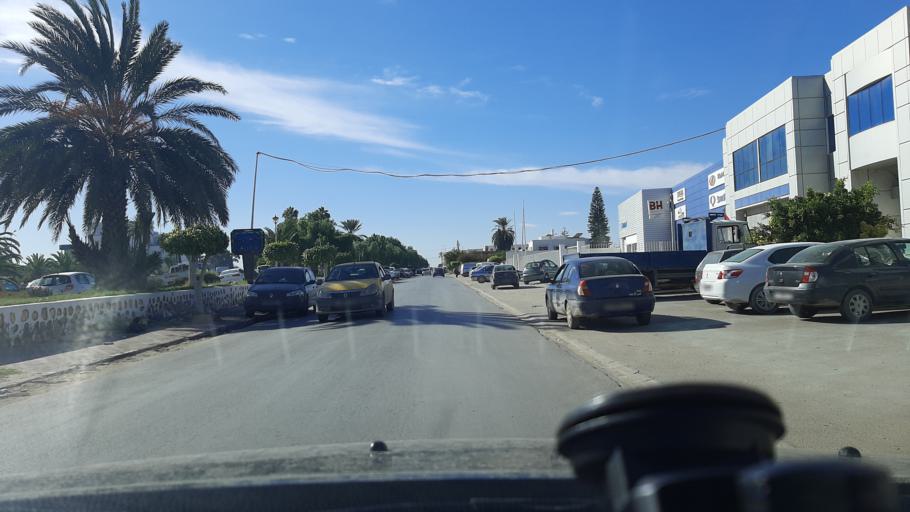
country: TN
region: Safaqis
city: Sfax
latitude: 34.7213
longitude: 10.7334
